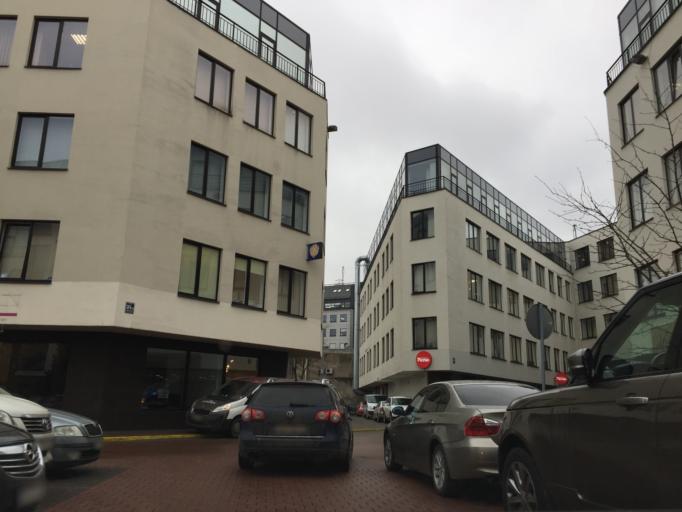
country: LV
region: Riga
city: Riga
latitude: 56.9668
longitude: 24.1417
